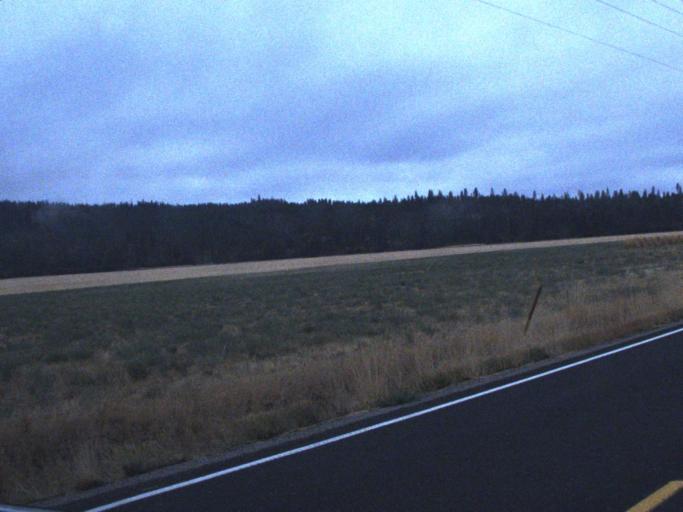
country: US
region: Washington
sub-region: Spokane County
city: Deer Park
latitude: 47.9228
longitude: -117.7837
